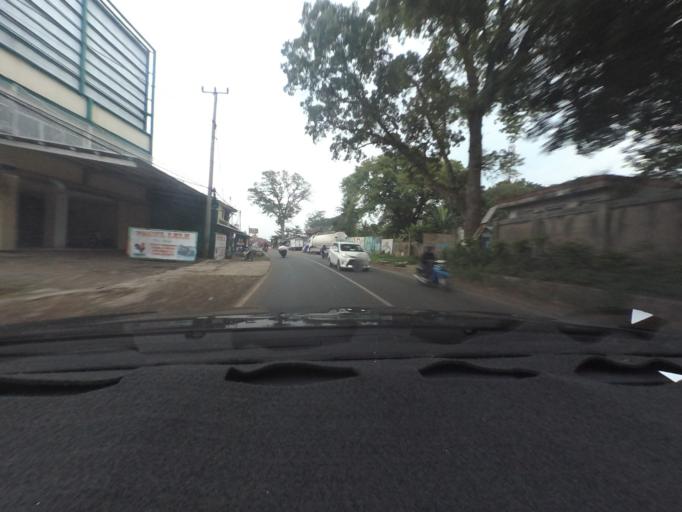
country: ID
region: West Java
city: Cicurug
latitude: -6.8055
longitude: 106.7719
